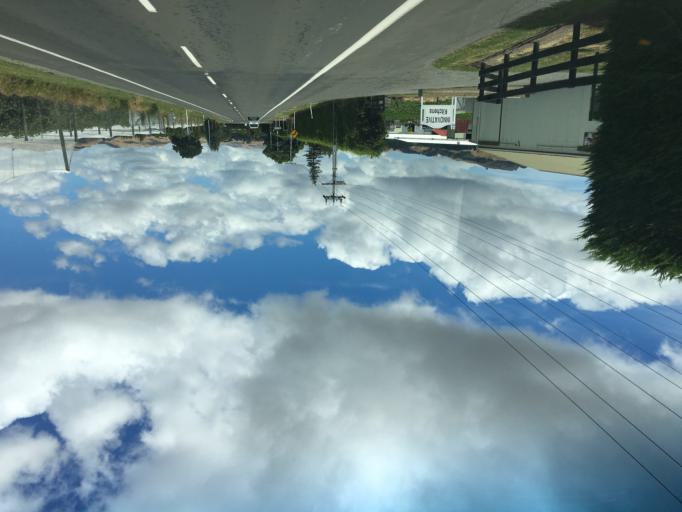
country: NZ
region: Hawke's Bay
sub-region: Hastings District
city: Hastings
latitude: -39.6542
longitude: 176.8873
